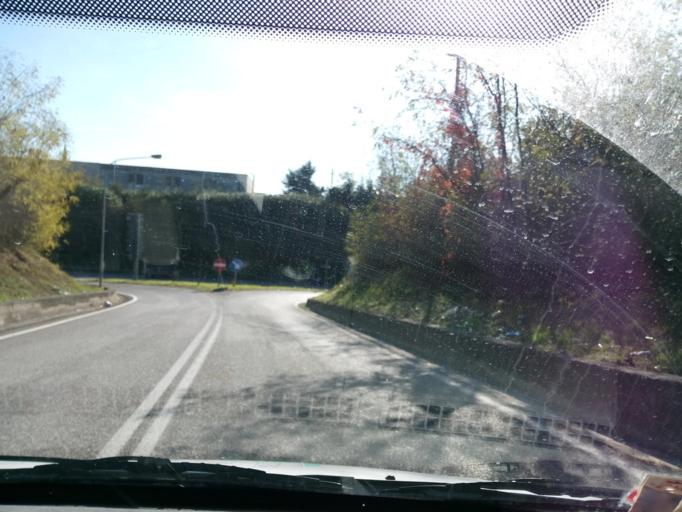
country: IT
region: Veneto
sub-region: Provincia di Vicenza
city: San Zeno-San Giuseppe
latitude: 45.7375
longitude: 11.7574
